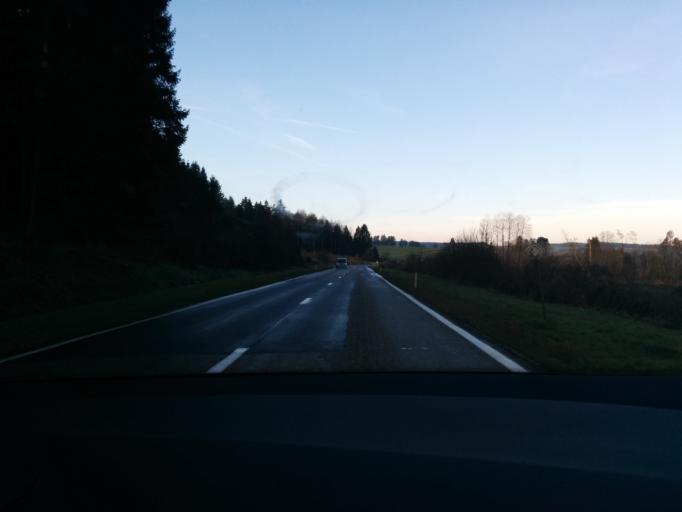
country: BE
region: Wallonia
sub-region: Province du Luxembourg
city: Gouvy
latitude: 50.2212
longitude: 5.9449
